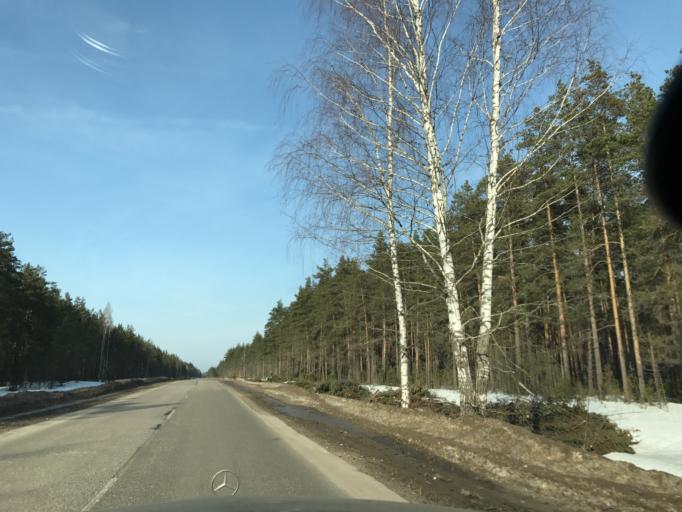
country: RU
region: Vladimir
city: Galitsy
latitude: 56.0399
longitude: 42.8628
